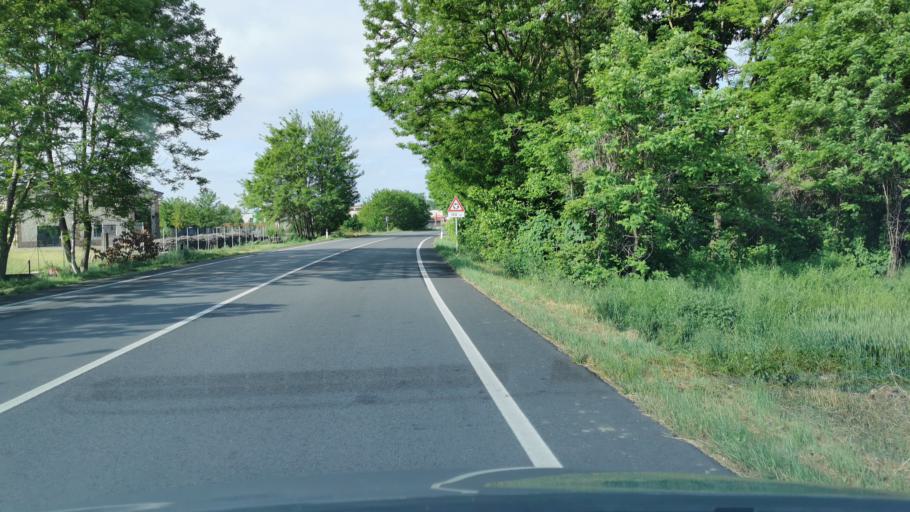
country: IT
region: Piedmont
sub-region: Provincia di Torino
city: Santena
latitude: 44.9417
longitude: 7.7803
